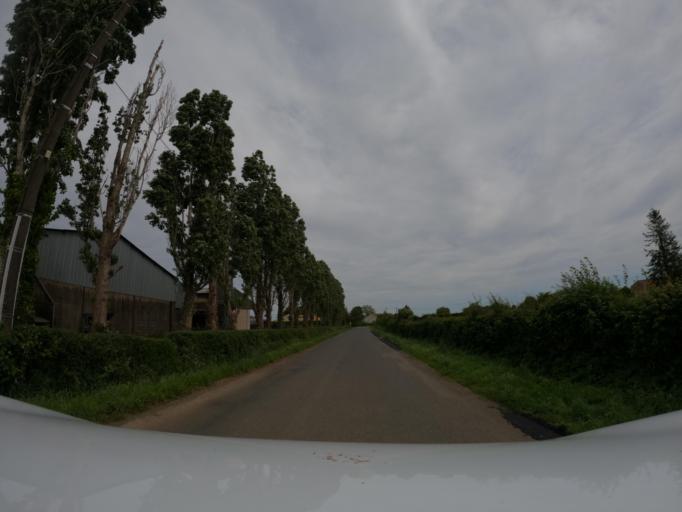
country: FR
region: Pays de la Loire
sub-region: Departement de la Vendee
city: Saint-Hilaire-des-Loges
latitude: 46.4929
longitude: -0.6333
